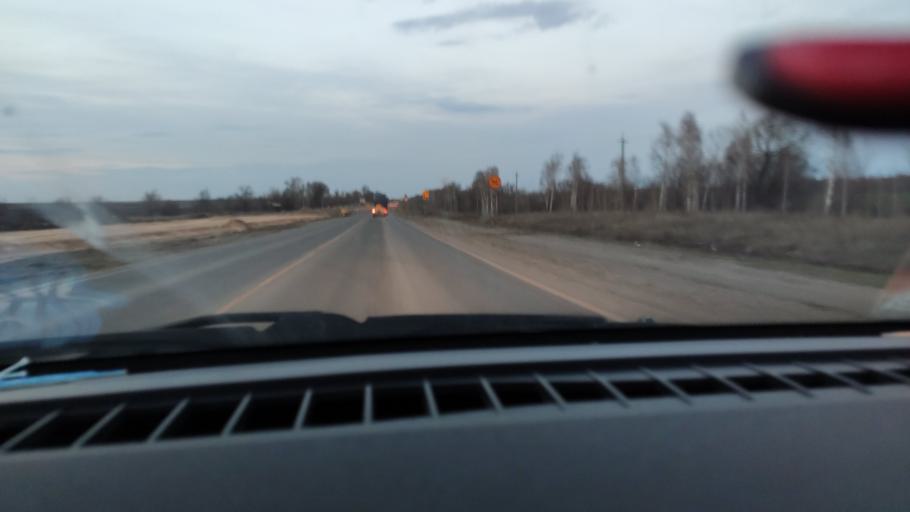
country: RU
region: Saratov
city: Sinodskoye
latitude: 52.0199
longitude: 46.7046
